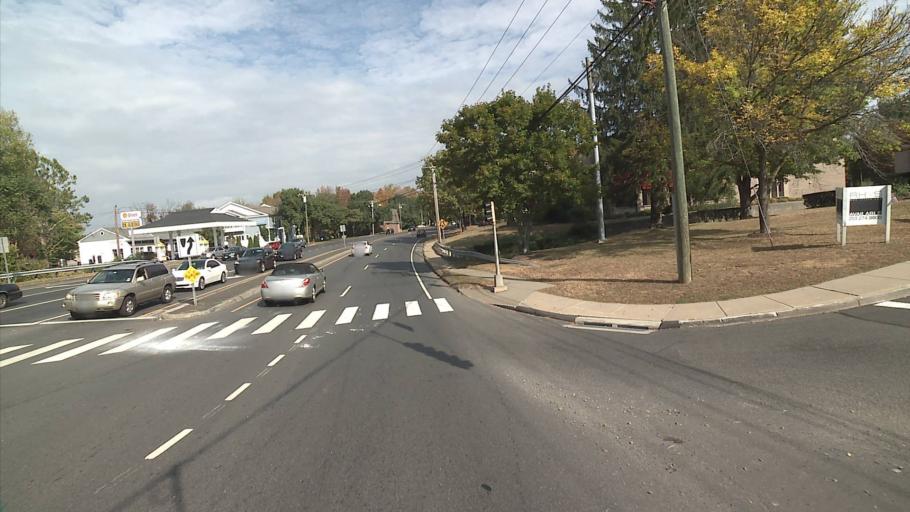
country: US
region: Connecticut
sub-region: New Haven County
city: Southbury
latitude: 41.4795
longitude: -73.2133
